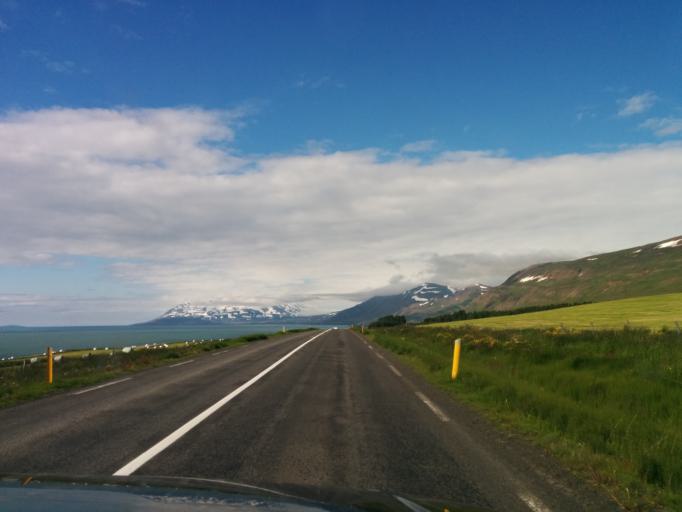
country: IS
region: Northeast
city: Akureyri
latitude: 65.7588
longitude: -18.0734
